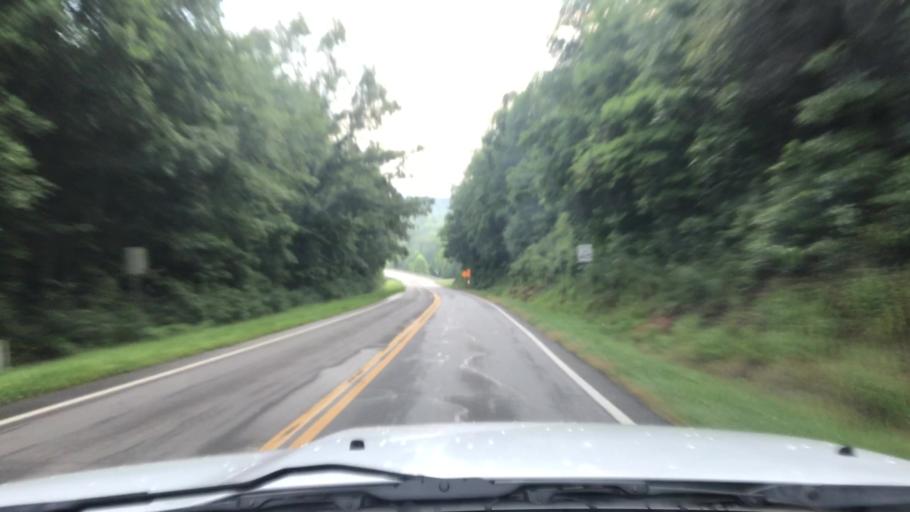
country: US
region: Georgia
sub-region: Fannin County
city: Blue Ridge
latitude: 34.9202
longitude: -84.2727
